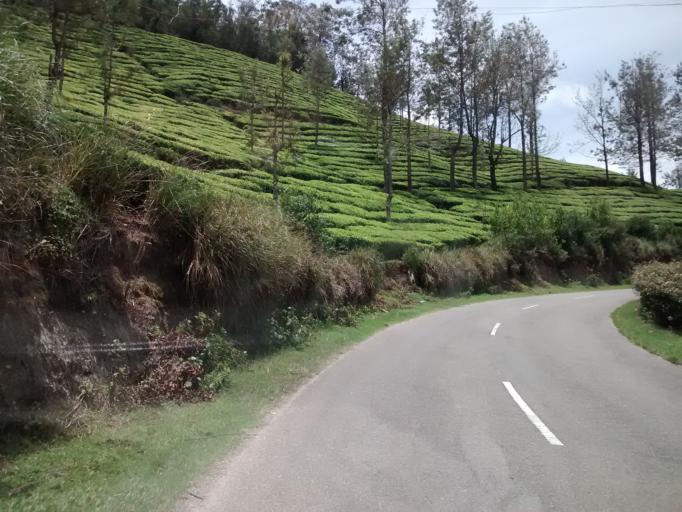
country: IN
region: Kerala
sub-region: Idukki
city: Munnar
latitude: 10.1291
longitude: 77.2157
